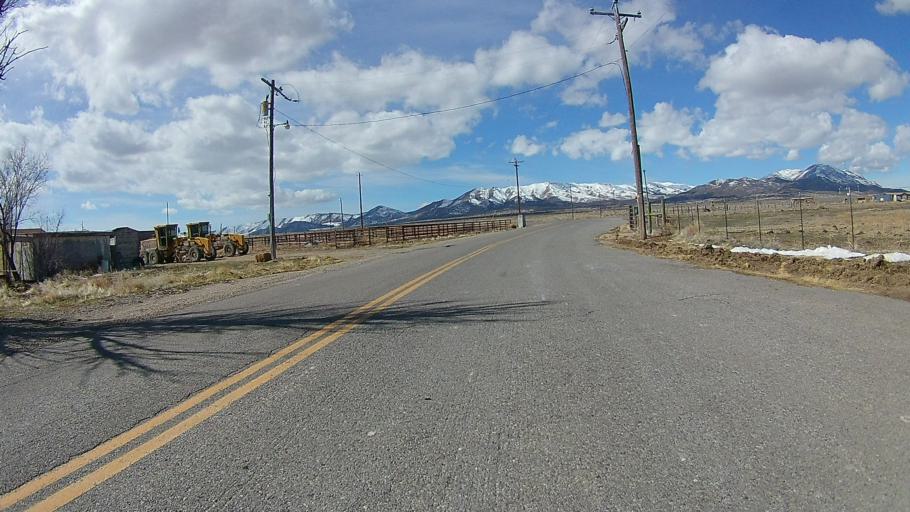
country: US
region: Utah
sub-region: Tooele County
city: Tooele
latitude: 40.1737
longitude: -112.4264
